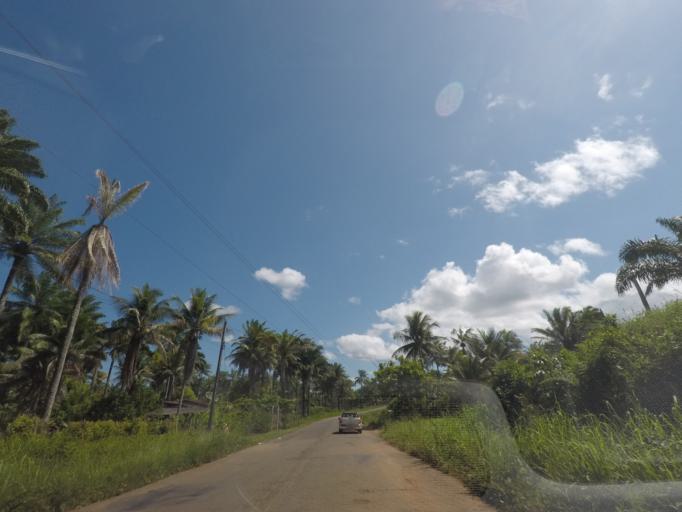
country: BR
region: Bahia
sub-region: Taperoa
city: Taperoa
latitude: -13.5610
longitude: -39.1049
